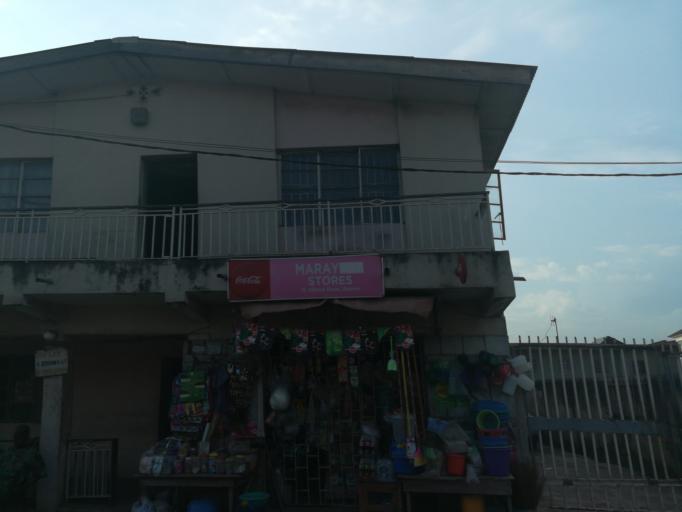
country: NG
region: Lagos
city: Ojota
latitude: 6.5869
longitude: 3.3943
